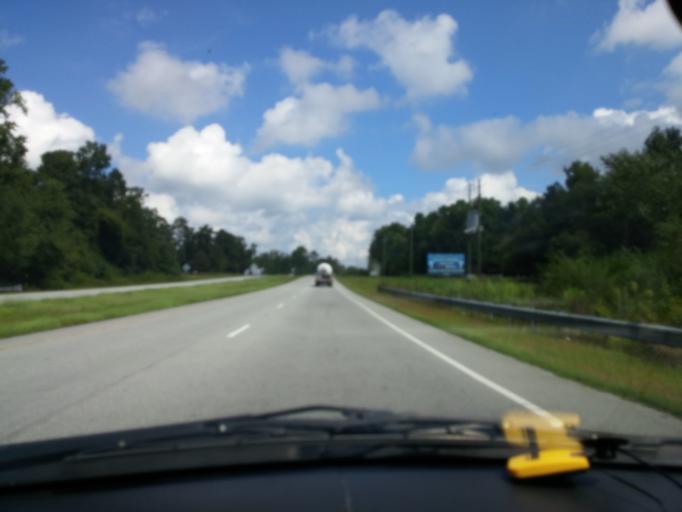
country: US
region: North Carolina
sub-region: Duplin County
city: Beulaville
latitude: 35.0813
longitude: -77.7318
